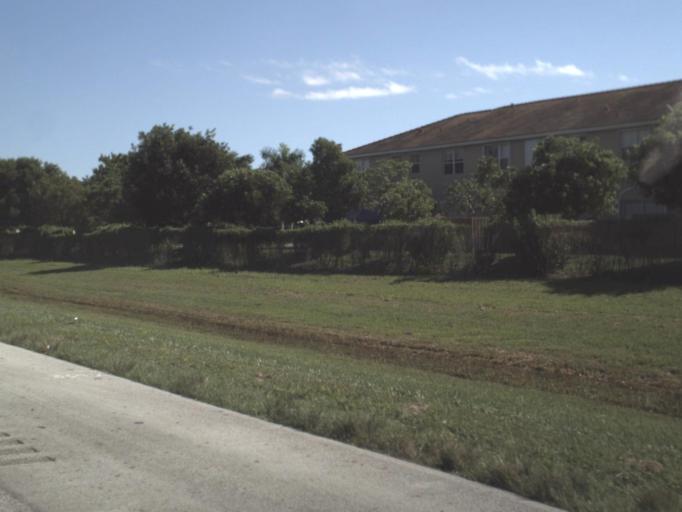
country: US
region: Florida
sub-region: Miami-Dade County
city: Leisure City
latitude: 25.4811
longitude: -80.4334
